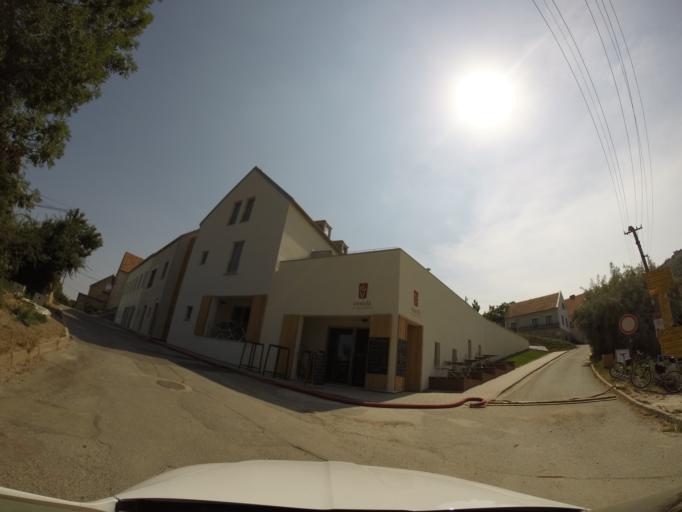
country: CZ
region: South Moravian
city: Sakvice
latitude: 48.8758
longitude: 16.6690
